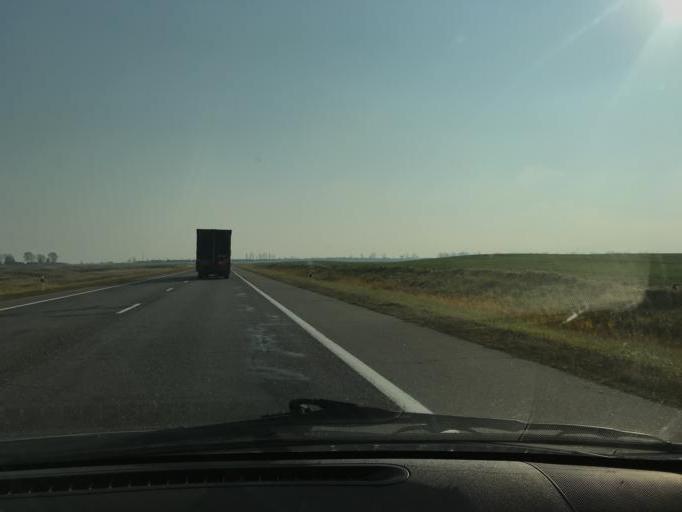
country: BY
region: Vitebsk
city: Chashniki
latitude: 55.0108
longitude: 29.1256
